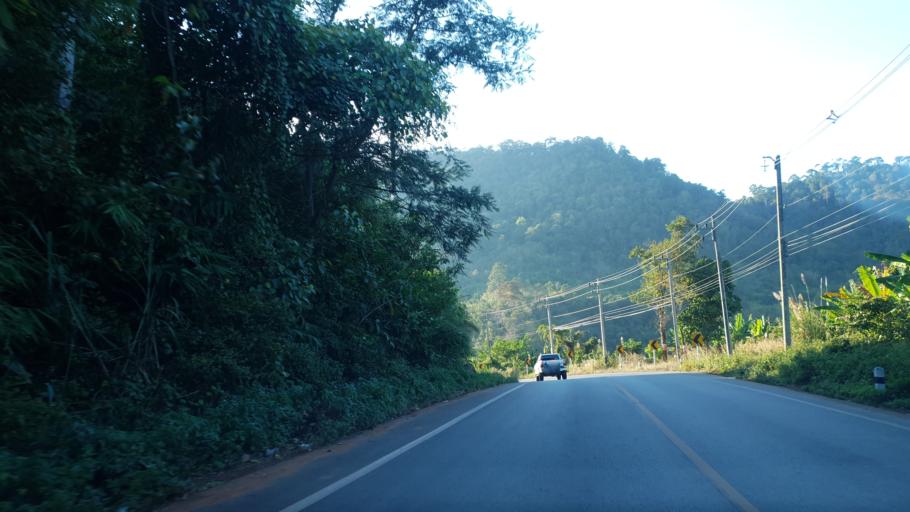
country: TH
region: Loei
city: Dan Sai
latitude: 17.2246
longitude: 101.0311
